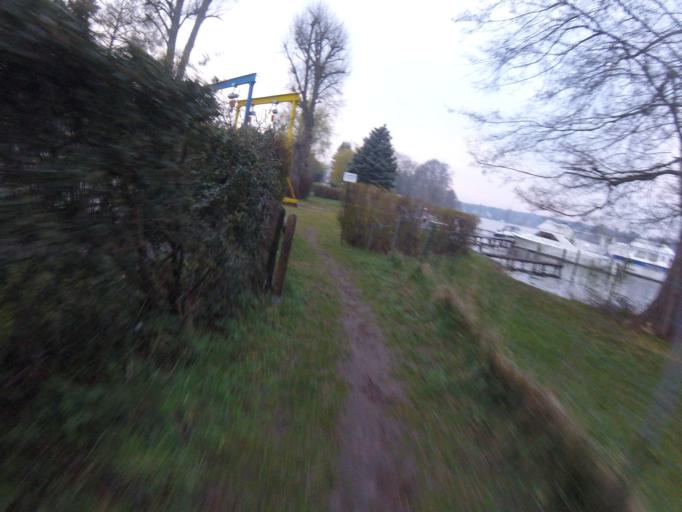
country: DE
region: Brandenburg
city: Konigs Wusterhausen
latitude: 52.2908
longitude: 13.6753
